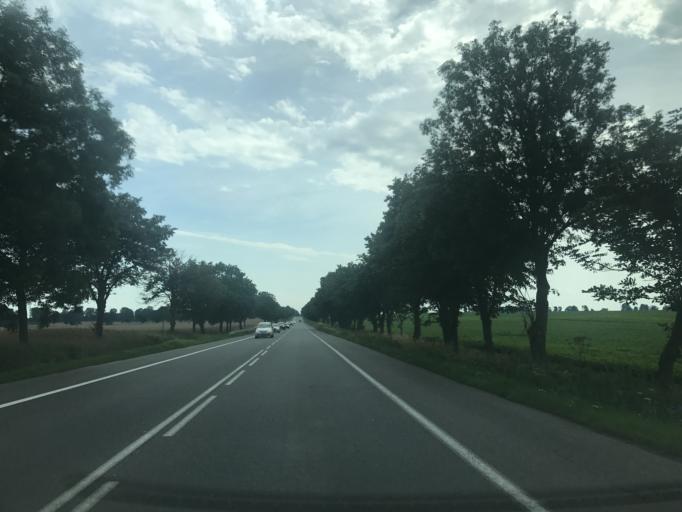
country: PL
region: Warmian-Masurian Voivodeship
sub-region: Powiat ostrodzki
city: Gierzwald
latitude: 53.6397
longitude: 20.0555
